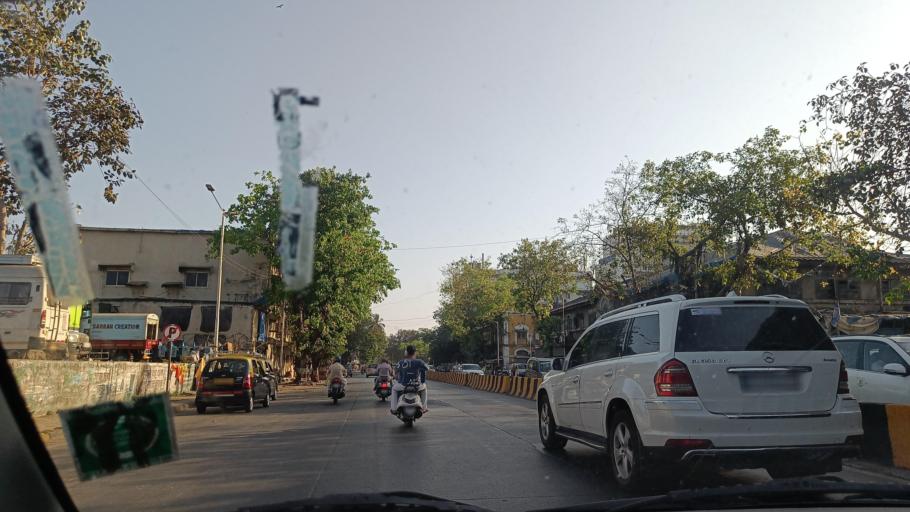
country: IN
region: Maharashtra
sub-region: Raigarh
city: Uran
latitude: 18.9508
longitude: 72.8411
